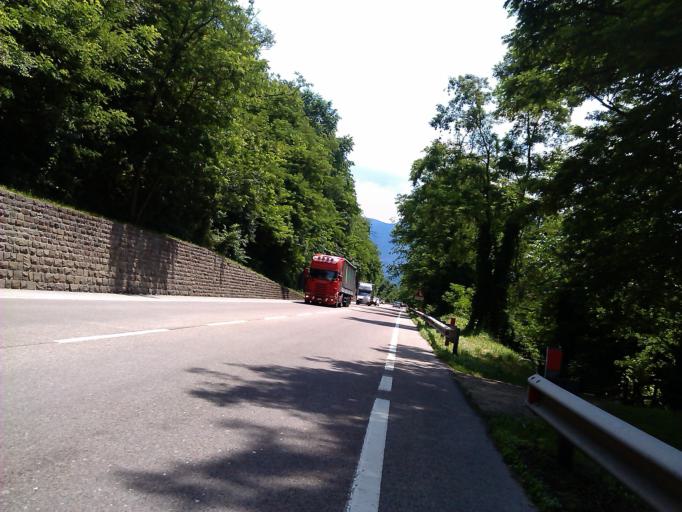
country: IT
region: Trentino-Alto Adige
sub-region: Provincia di Trento
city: Tenna
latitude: 46.0233
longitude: 11.2477
